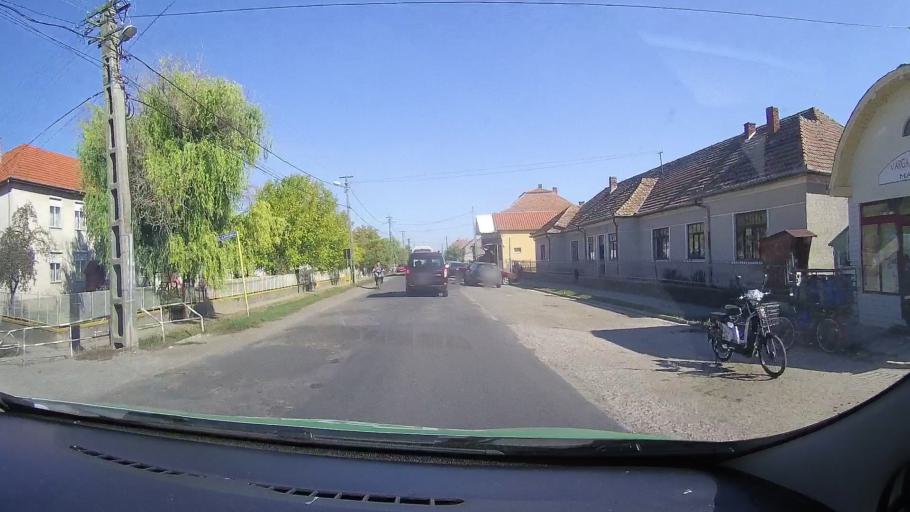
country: RO
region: Satu Mare
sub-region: Comuna Capleni
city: Capleni
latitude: 47.7048
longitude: 22.4971
